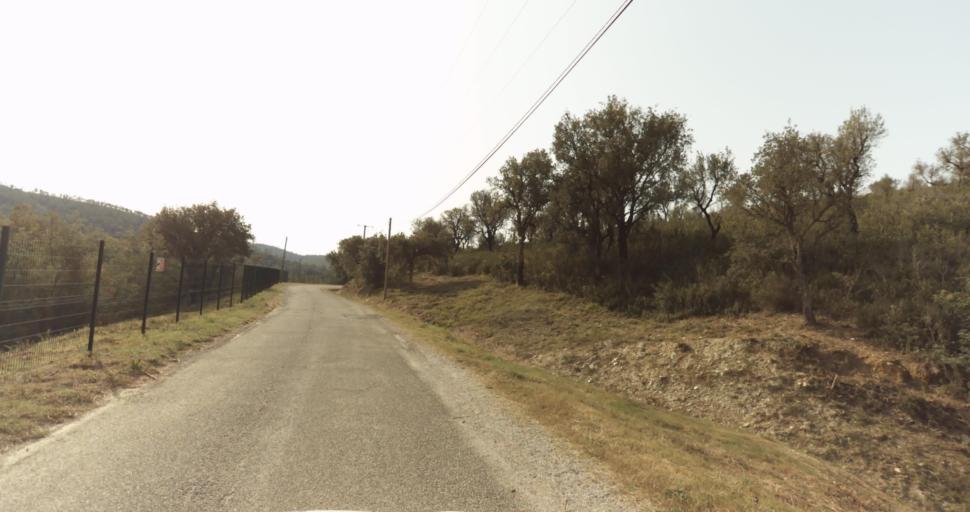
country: FR
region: Provence-Alpes-Cote d'Azur
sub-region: Departement du Var
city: Bormes-les-Mimosas
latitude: 43.1475
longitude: 6.2923
